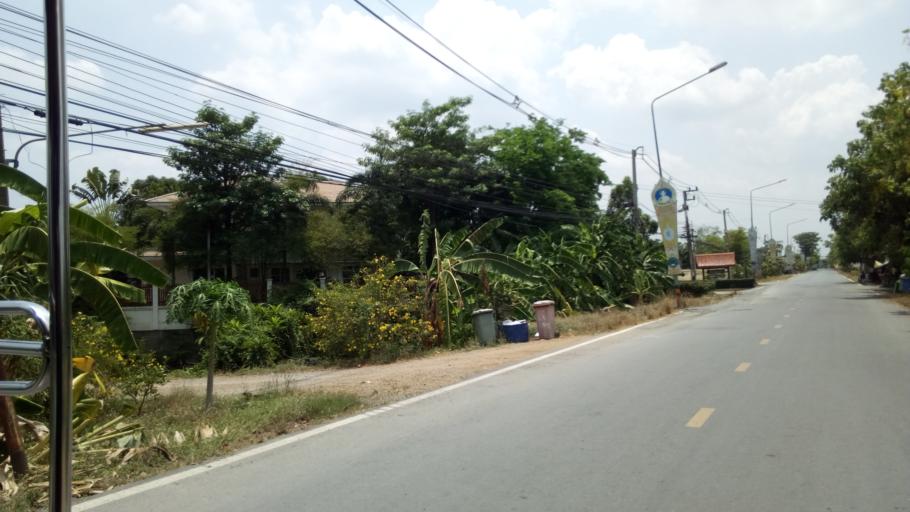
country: TH
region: Pathum Thani
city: Sam Khok
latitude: 14.0995
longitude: 100.5351
